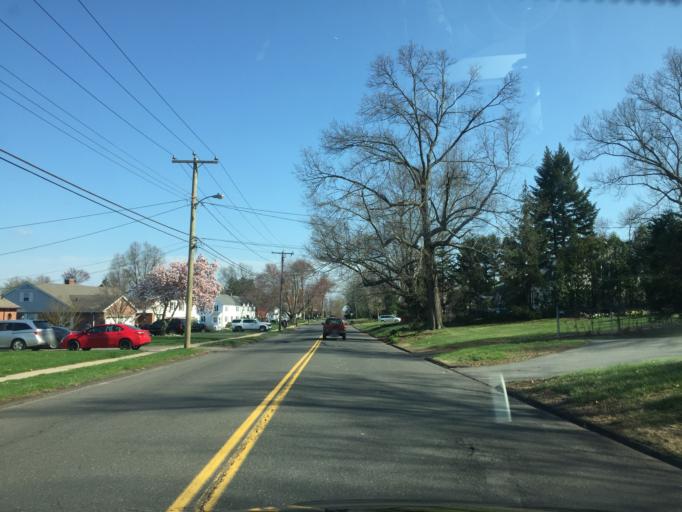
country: US
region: Connecticut
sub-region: Hartford County
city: Wethersfield
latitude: 41.6963
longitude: -72.6830
